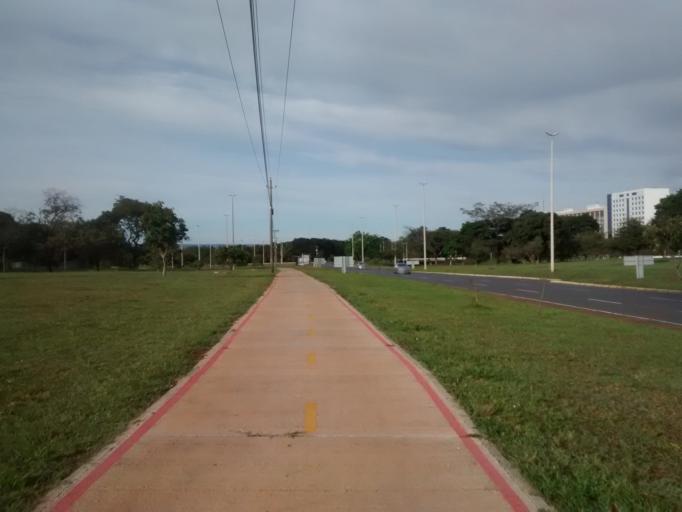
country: BR
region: Federal District
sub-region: Brasilia
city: Brasilia
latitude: -15.8000
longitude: -47.8764
